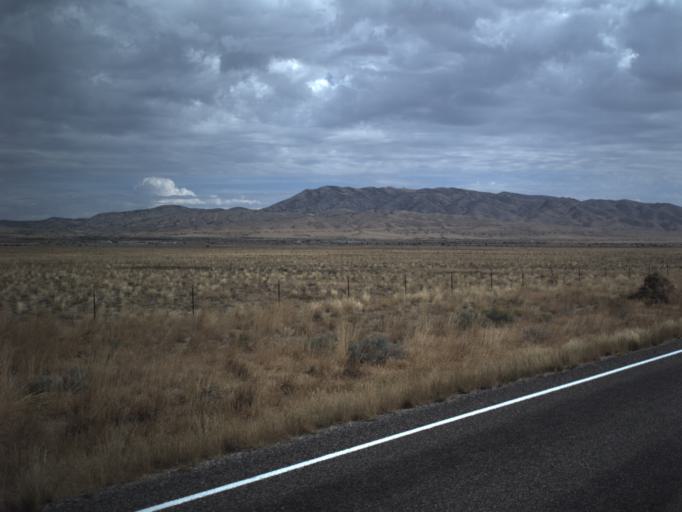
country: US
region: Utah
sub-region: Tooele County
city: Wendover
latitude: 41.4318
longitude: -113.7915
